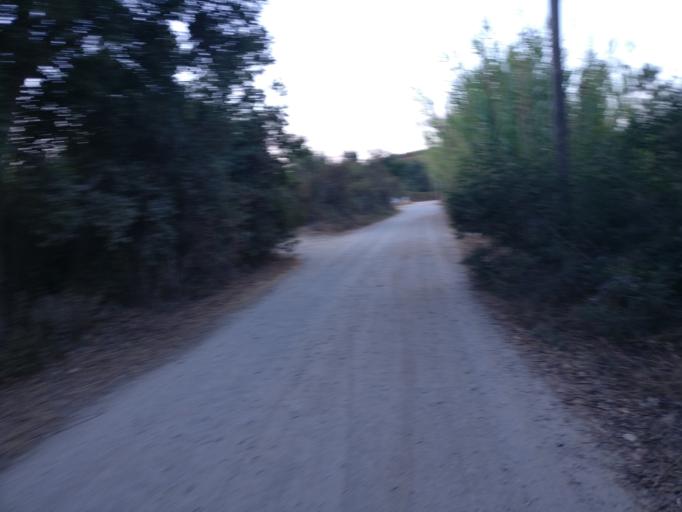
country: PT
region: Beja
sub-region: Odemira
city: Odemira
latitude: 37.7150
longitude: -8.5161
